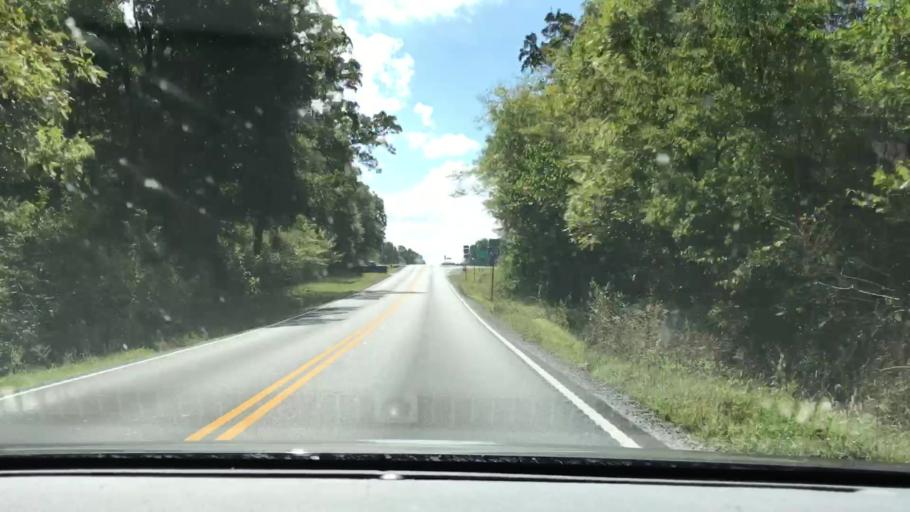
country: US
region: Kentucky
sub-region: Graves County
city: Mayfield
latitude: 36.7785
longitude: -88.5959
